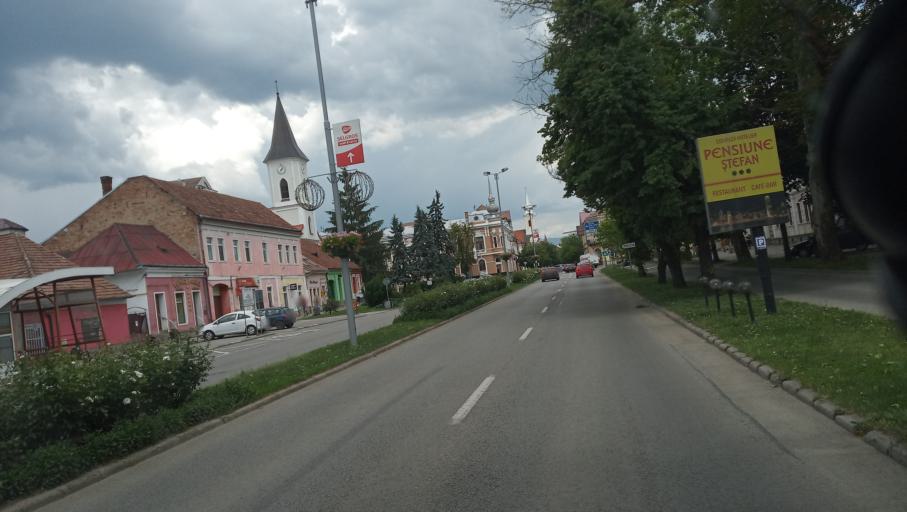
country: RO
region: Bistrita-Nasaud
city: Bistrita
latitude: 47.1295
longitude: 24.4899
